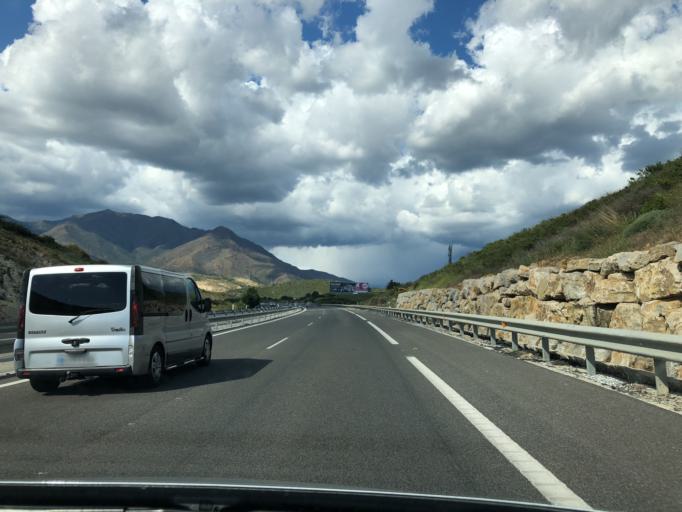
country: ES
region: Andalusia
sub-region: Provincia de Malaga
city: Manilva
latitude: 36.4111
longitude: -5.2234
